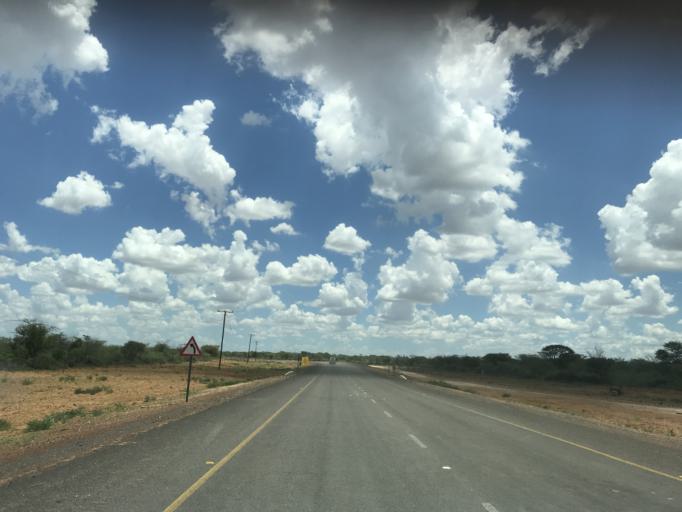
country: BW
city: Mabuli
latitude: -25.8008
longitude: 24.7124
